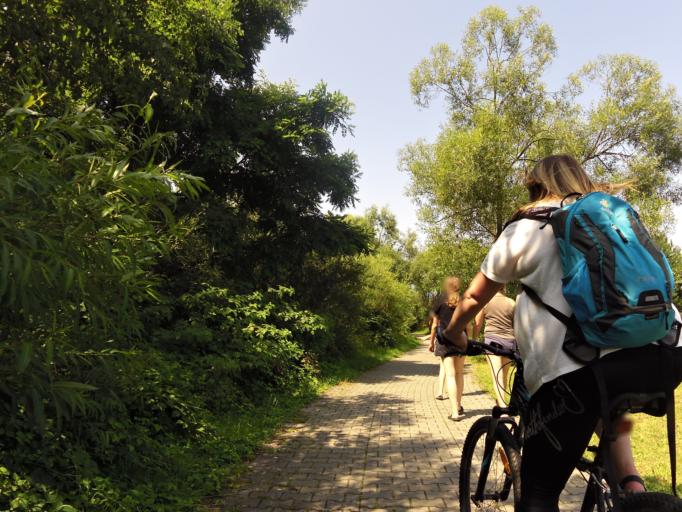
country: PL
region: Silesian Voivodeship
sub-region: Powiat zywiecki
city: Milowka
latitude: 49.5510
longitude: 19.0911
